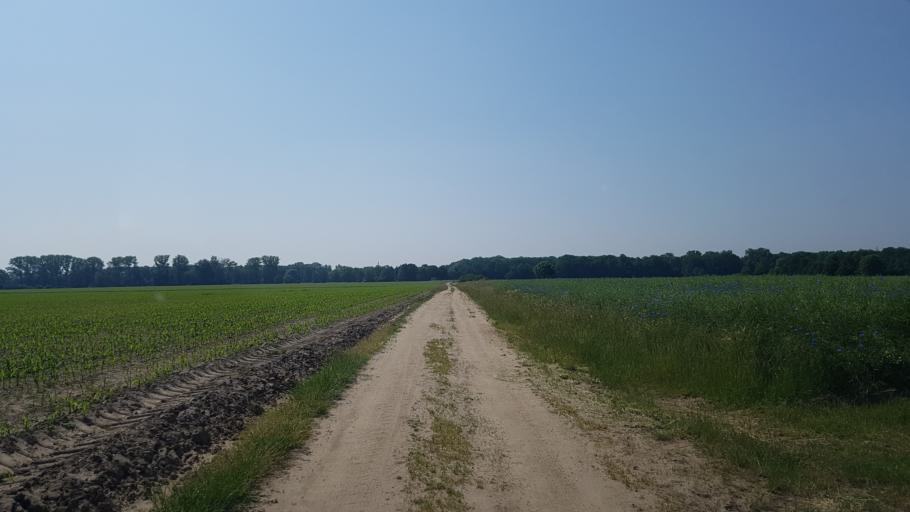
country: DE
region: Brandenburg
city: Sonnewalde
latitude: 51.7113
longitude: 13.6421
